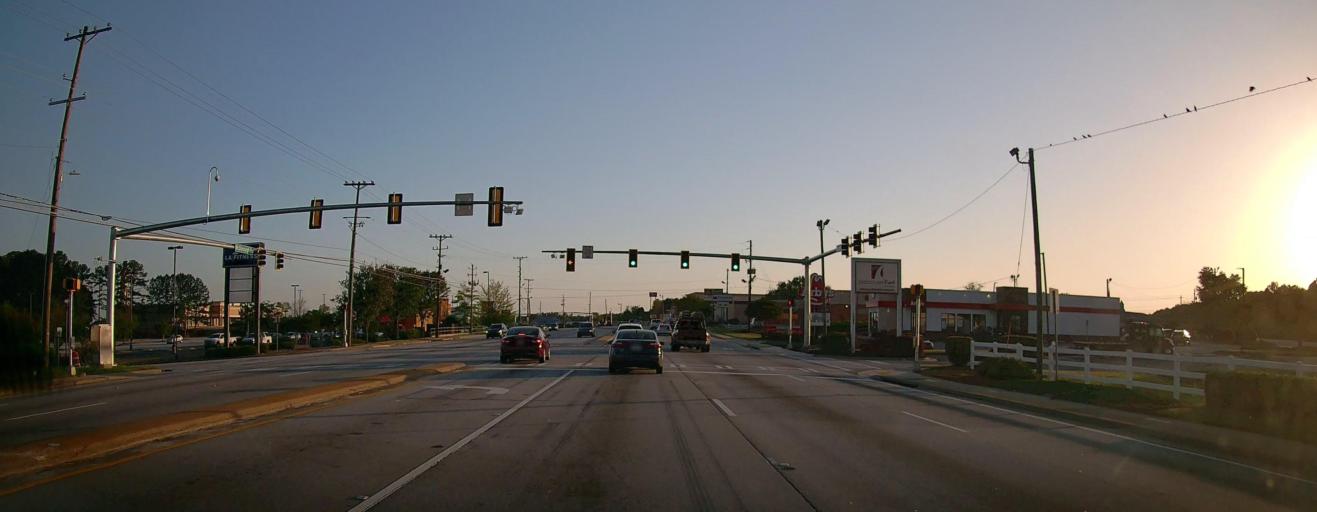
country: US
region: Georgia
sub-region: Rockdale County
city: Conyers
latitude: 33.6481
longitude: -84.0116
